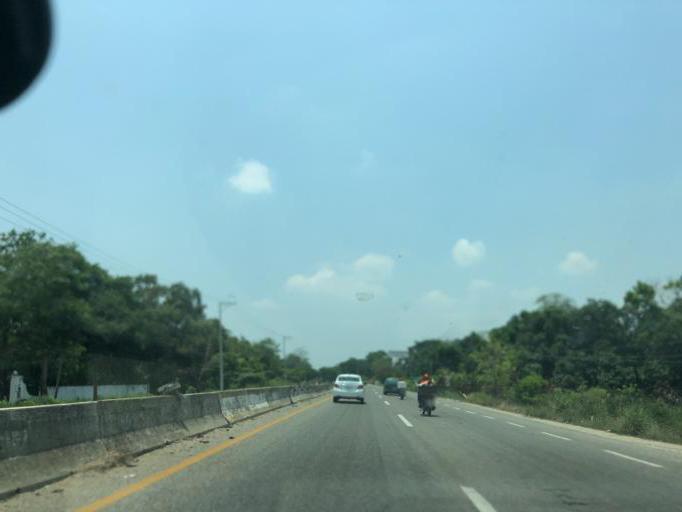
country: MX
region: Tabasco
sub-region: Centro
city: Gaviotas Sur (El Cedral)
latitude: 17.9624
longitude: -92.9155
